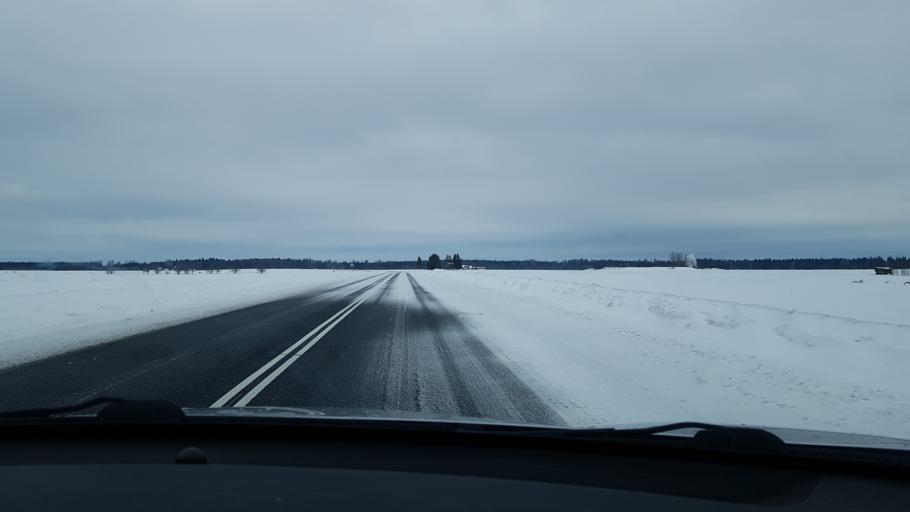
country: EE
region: Jaervamaa
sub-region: Jaerva-Jaani vald
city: Jarva-Jaani
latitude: 59.1156
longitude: 25.7935
